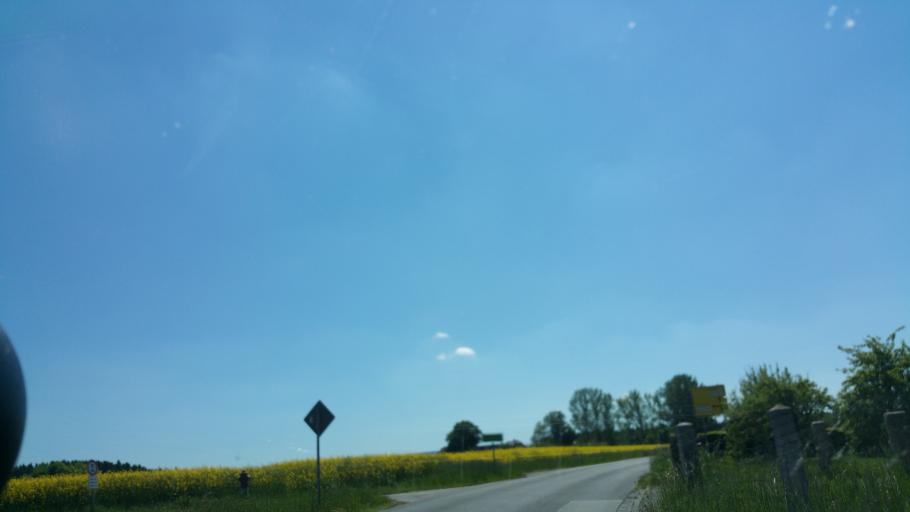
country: DE
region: Bavaria
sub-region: Upper Franconia
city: Schwarzenbach an der Saale
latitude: 50.2062
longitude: 11.9321
